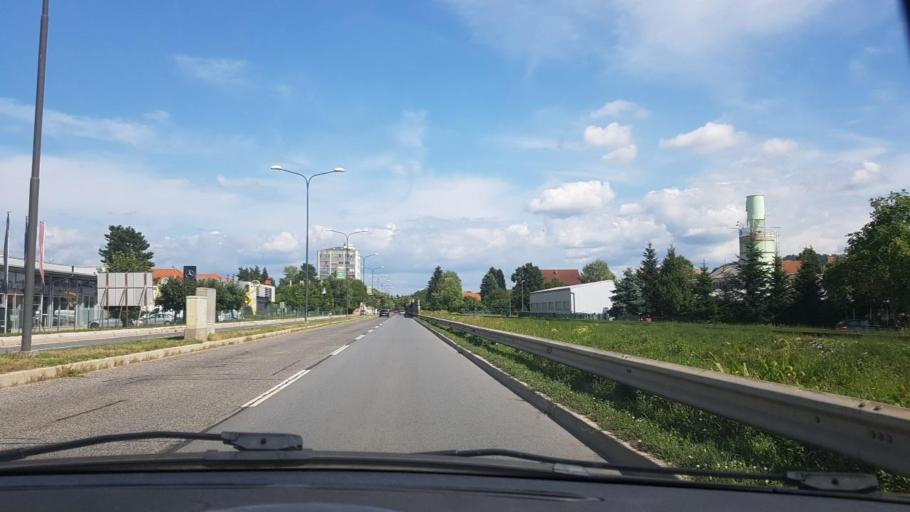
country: SI
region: Celje
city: Celje
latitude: 46.2368
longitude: 15.2572
